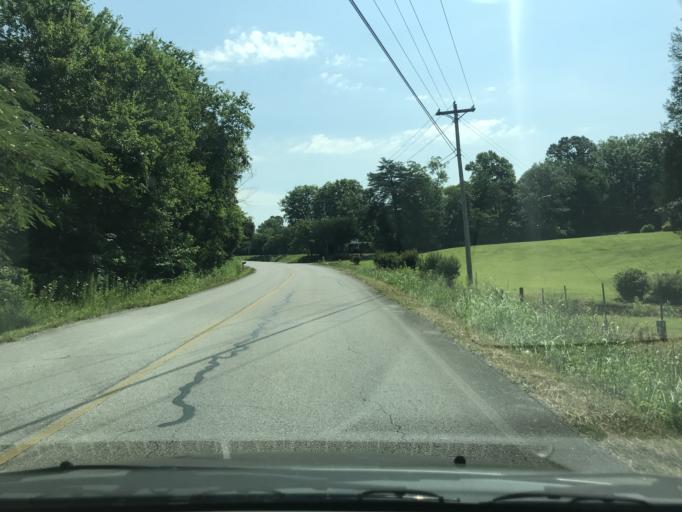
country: US
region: Tennessee
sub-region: Loudon County
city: Lenoir City
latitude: 35.8330
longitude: -84.3045
